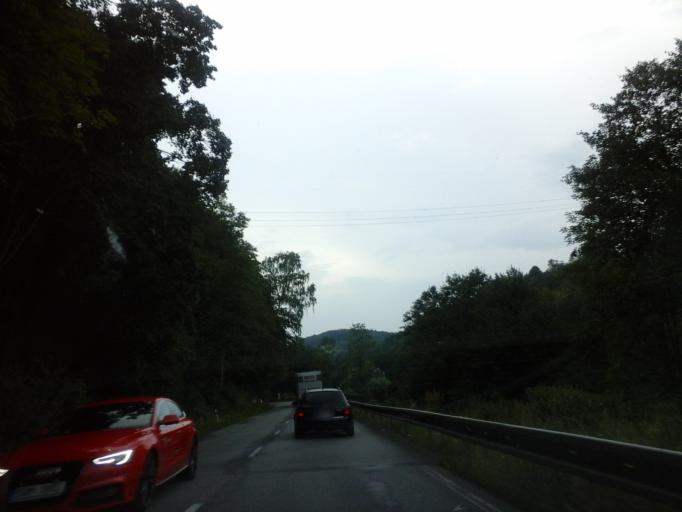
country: CZ
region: Pardubicky
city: Brnenec
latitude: 49.6084
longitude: 16.5317
